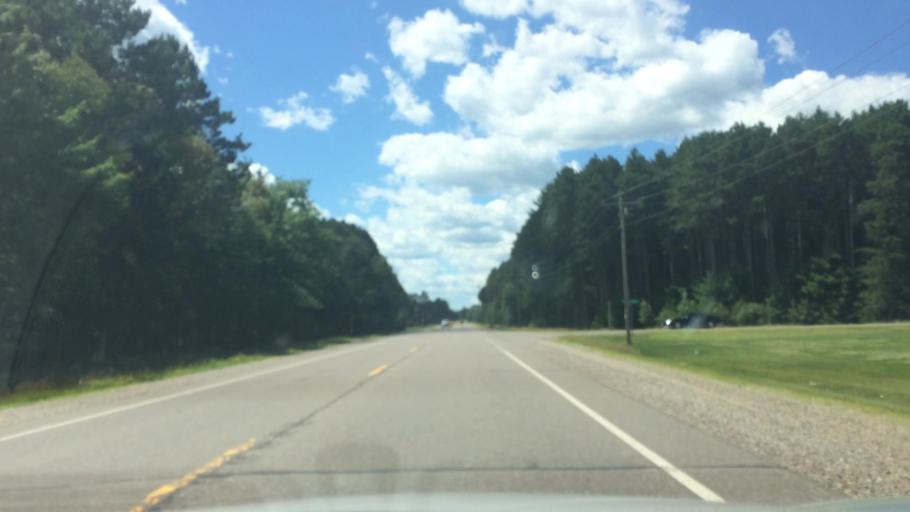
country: US
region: Wisconsin
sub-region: Vilas County
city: Lac du Flambeau
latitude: 45.8833
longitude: -89.7494
